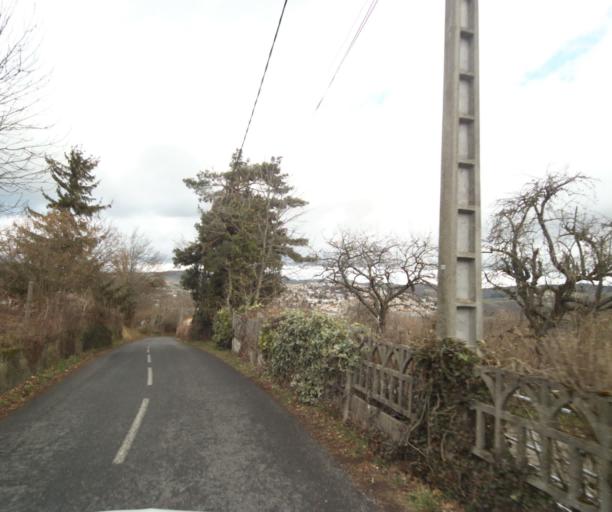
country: FR
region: Rhone-Alpes
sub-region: Departement de la Loire
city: Sorbiers
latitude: 45.4732
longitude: 4.4483
